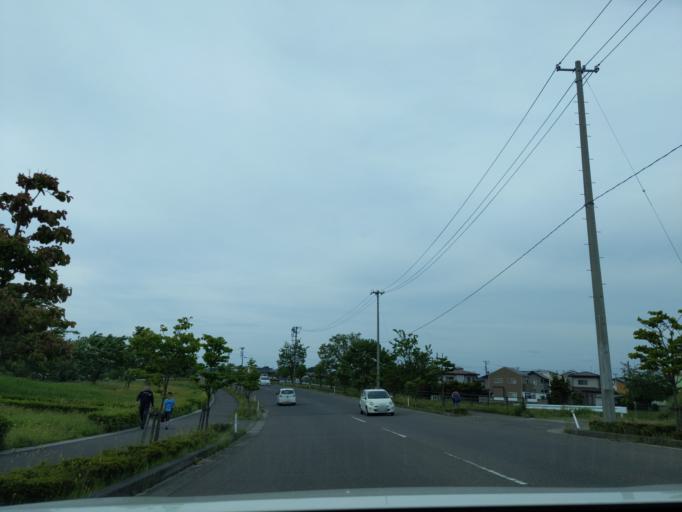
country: JP
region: Fukushima
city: Koriyama
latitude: 37.4172
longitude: 140.3337
